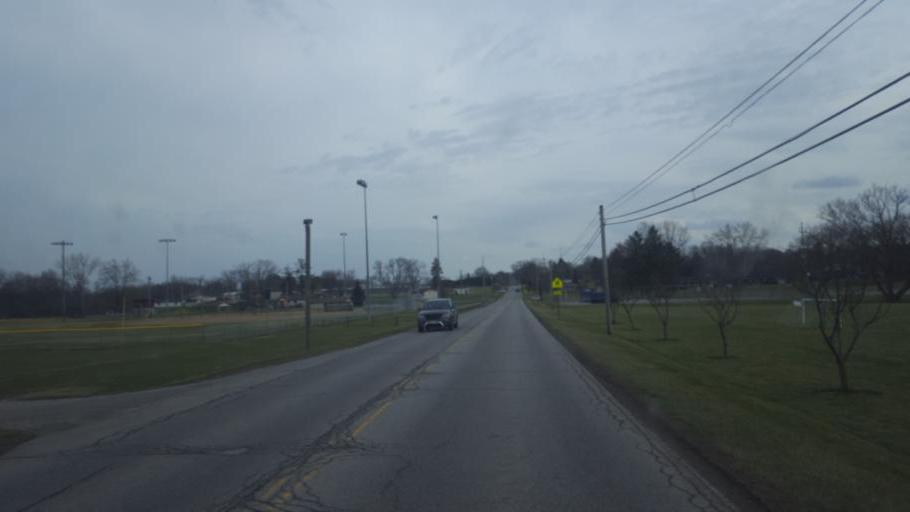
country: US
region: Ohio
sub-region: Richland County
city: Lexington
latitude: 40.6871
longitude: -82.5853
